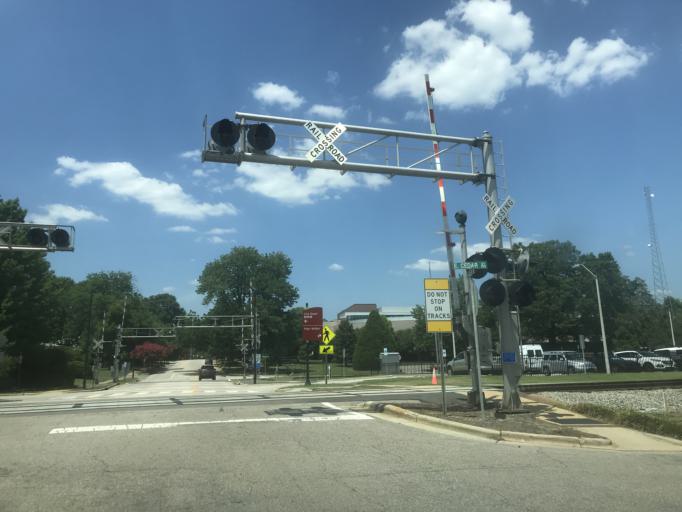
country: US
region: North Carolina
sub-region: Wake County
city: Cary
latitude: 35.7879
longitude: -78.7812
